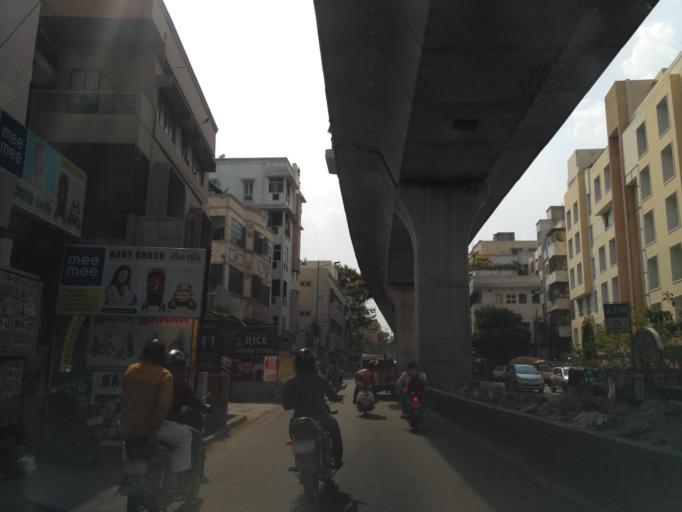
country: IN
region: Telangana
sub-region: Rangareddi
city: Kukatpalli
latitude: 17.4361
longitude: 78.4374
